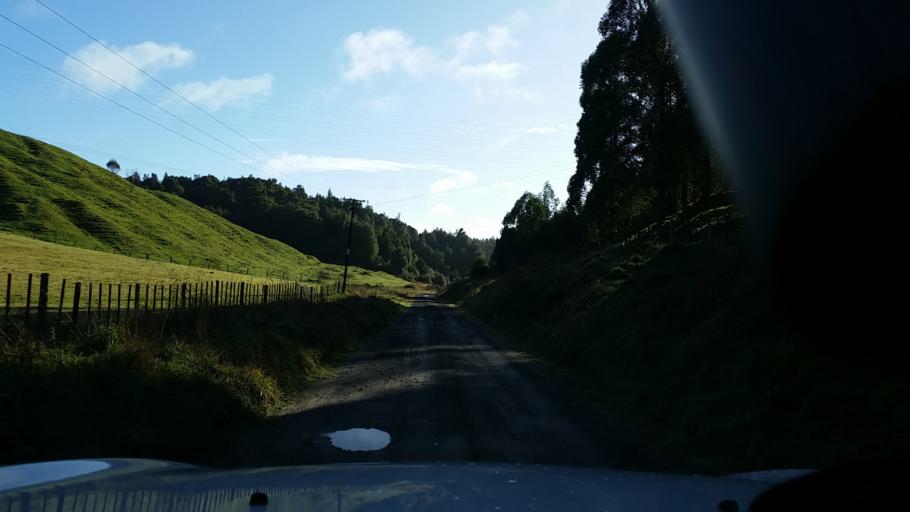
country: NZ
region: Bay of Plenty
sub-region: Kawerau District
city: Kawerau
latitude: -38.0129
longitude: 176.5973
